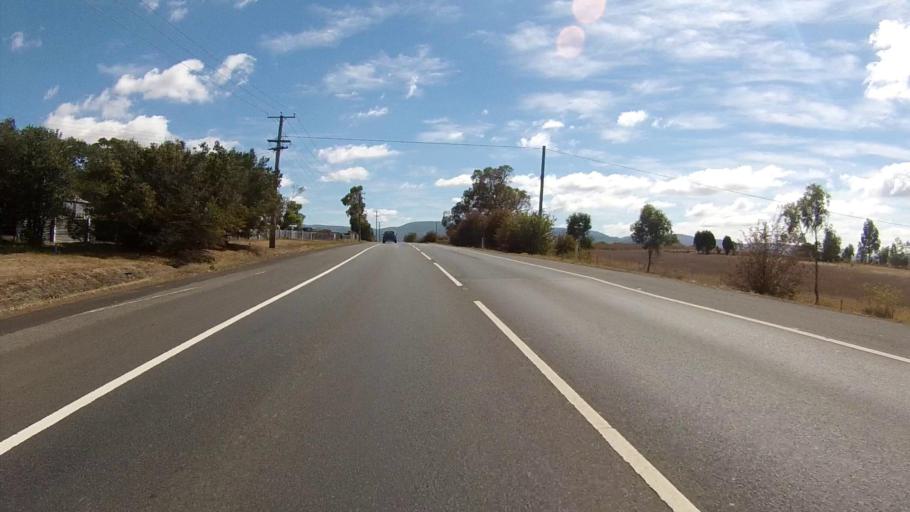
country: AU
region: Tasmania
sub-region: Brighton
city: Bridgewater
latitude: -42.7113
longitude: 147.2451
